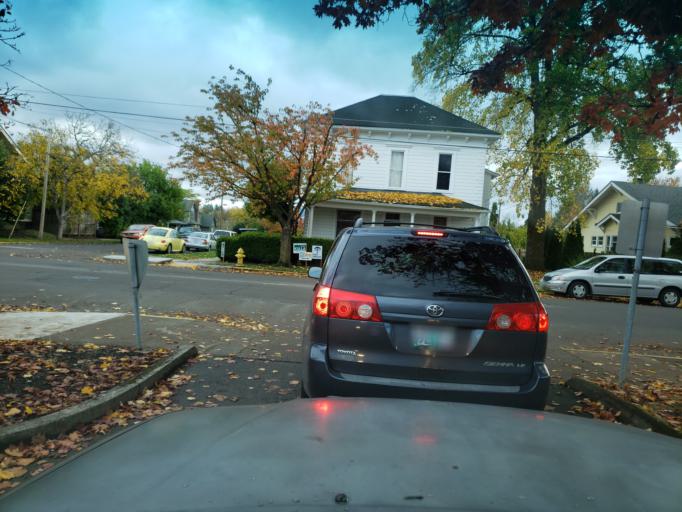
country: US
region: Oregon
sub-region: Yamhill County
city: McMinnville
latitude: 45.2088
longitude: -123.1923
